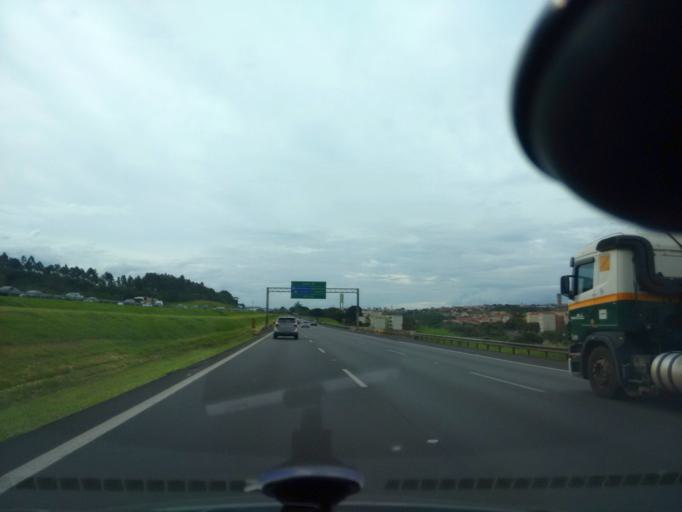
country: BR
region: Sao Paulo
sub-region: Campinas
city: Campinas
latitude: -22.9487
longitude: -47.1256
